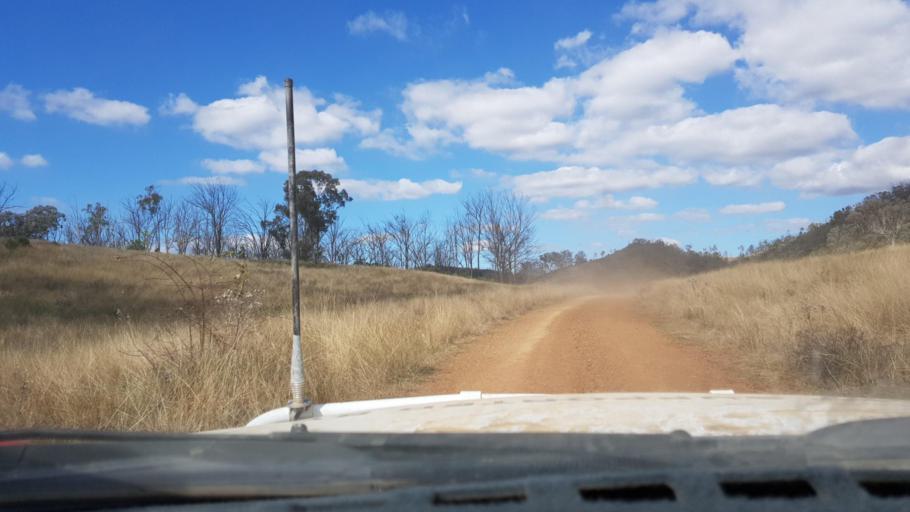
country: AU
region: New South Wales
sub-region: Tamworth Municipality
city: Manilla
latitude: -30.4364
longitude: 150.8274
